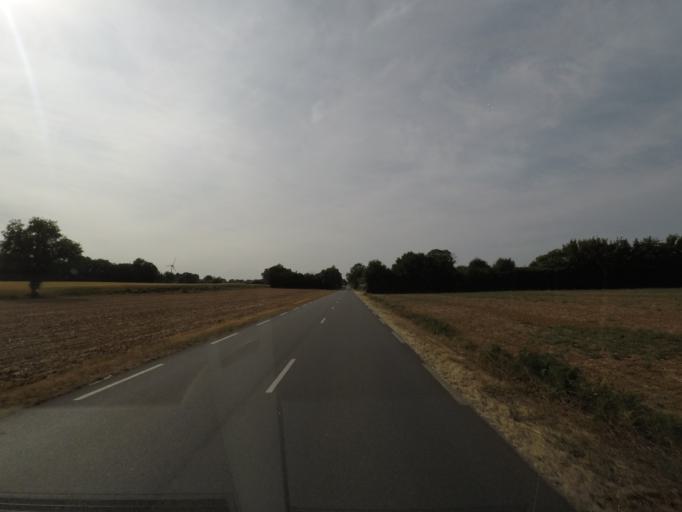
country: FR
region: Poitou-Charentes
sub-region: Departement des Deux-Sevres
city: Lezay
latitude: 46.1746
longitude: -0.0072
